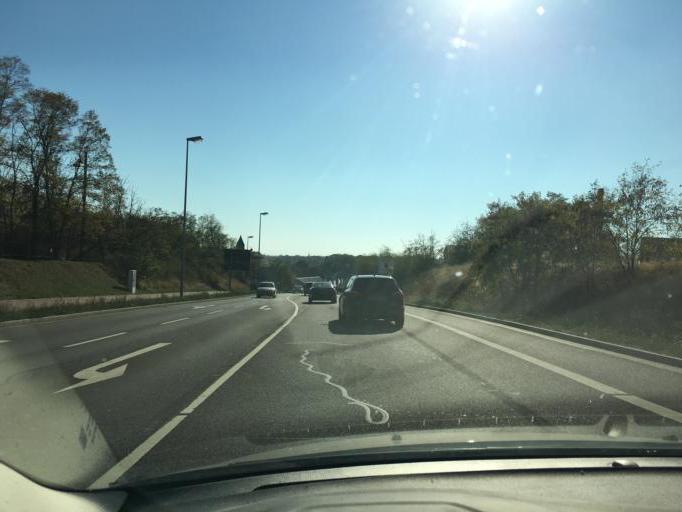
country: DE
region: Saxony-Anhalt
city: Bernburg
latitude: 51.8080
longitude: 11.7250
